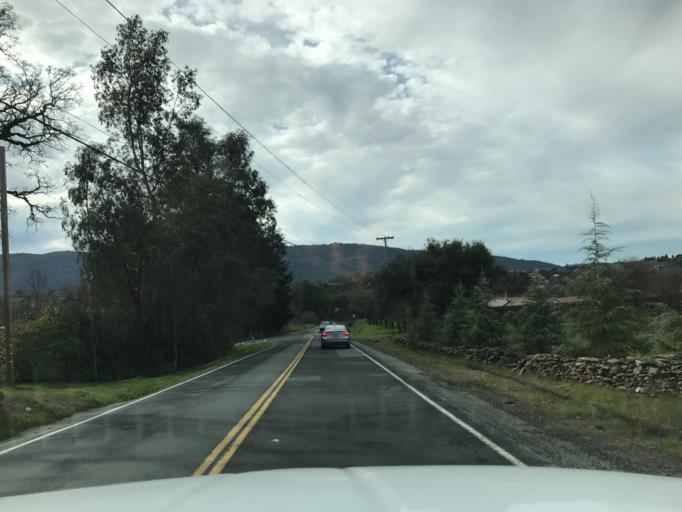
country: US
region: California
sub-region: Calaveras County
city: San Andreas
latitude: 38.1889
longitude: -120.6592
